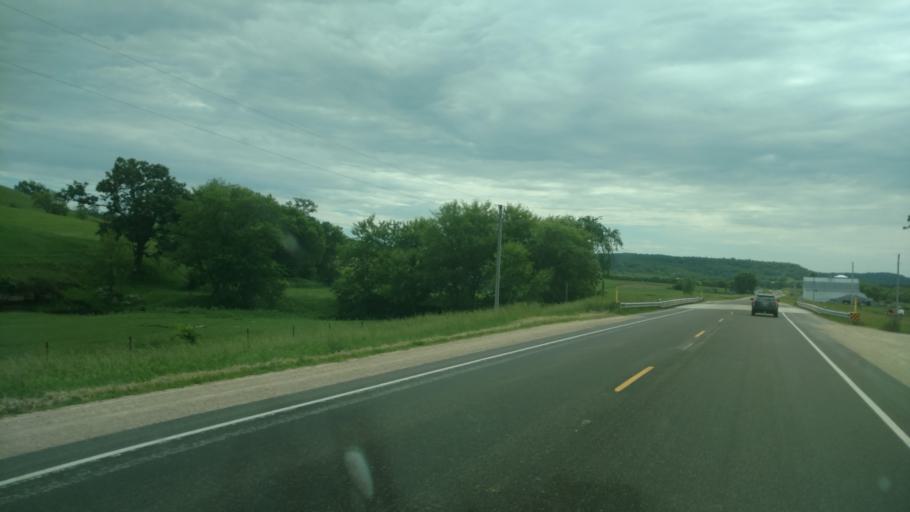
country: US
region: Wisconsin
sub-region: Monroe County
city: Tomah
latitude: 43.8485
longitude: -90.4737
